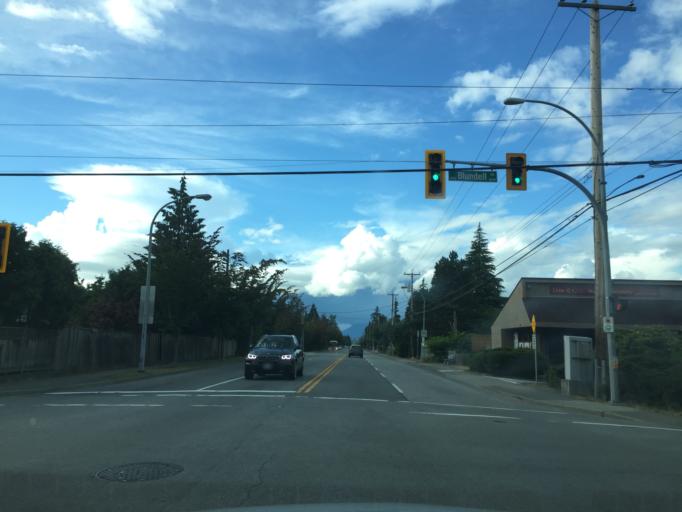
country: CA
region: British Columbia
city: Richmond
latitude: 49.1552
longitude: -123.1141
